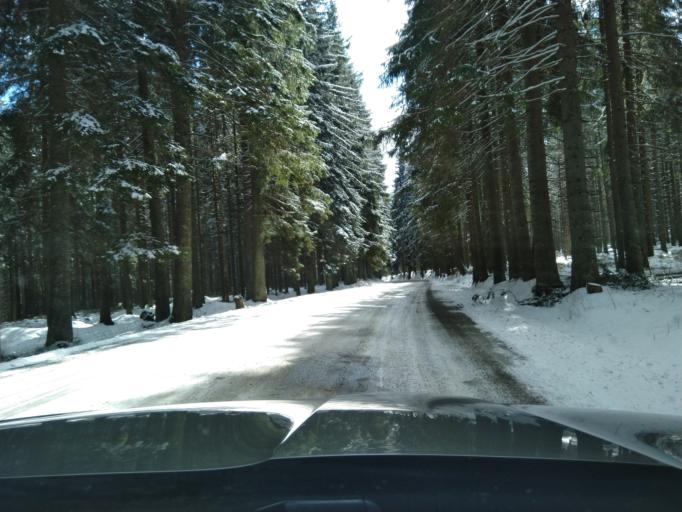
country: CZ
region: Jihocesky
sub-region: Okres Prachatice
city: Stachy
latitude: 49.0507
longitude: 13.6234
